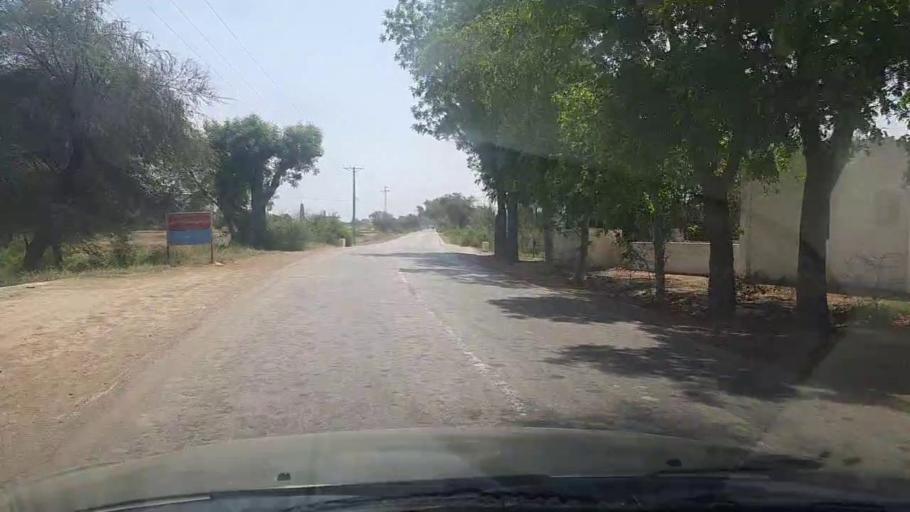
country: PK
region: Sindh
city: Hyderabad
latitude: 25.3796
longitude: 68.4537
